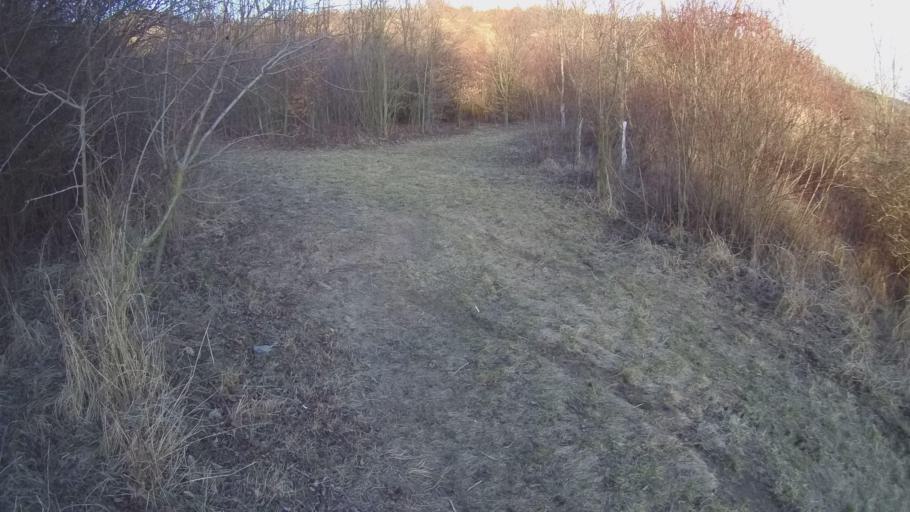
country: CZ
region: Ustecky
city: Roudnice nad Labem
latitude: 50.3781
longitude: 14.2854
